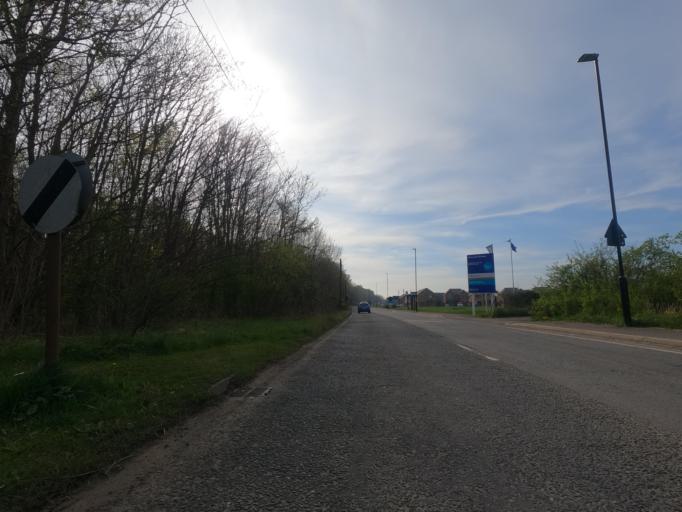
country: GB
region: England
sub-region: Newcastle upon Tyne
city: Hazlerigg
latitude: 55.0416
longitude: -1.6436
